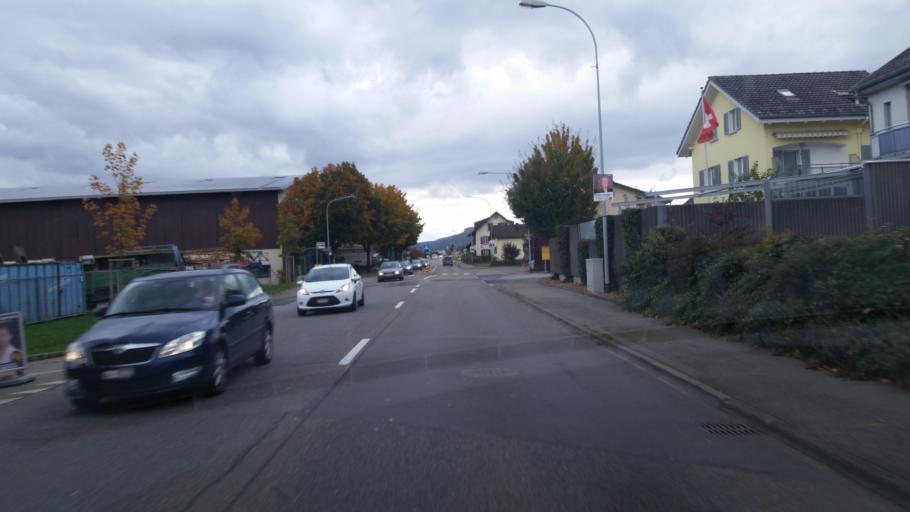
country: CH
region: Aargau
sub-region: Bezirk Baden
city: Obersiggenthal
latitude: 47.4932
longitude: 8.2768
